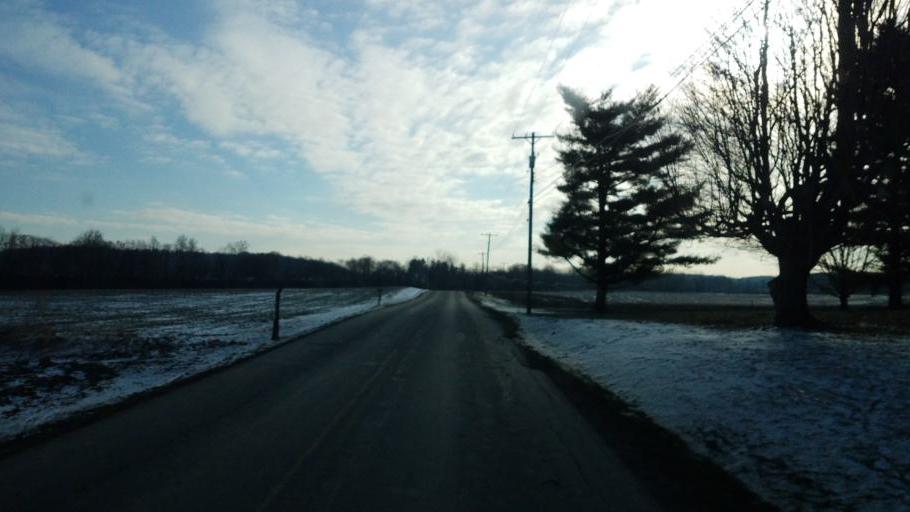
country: US
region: Ohio
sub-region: Richland County
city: Lexington
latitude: 40.6184
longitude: -82.5972
